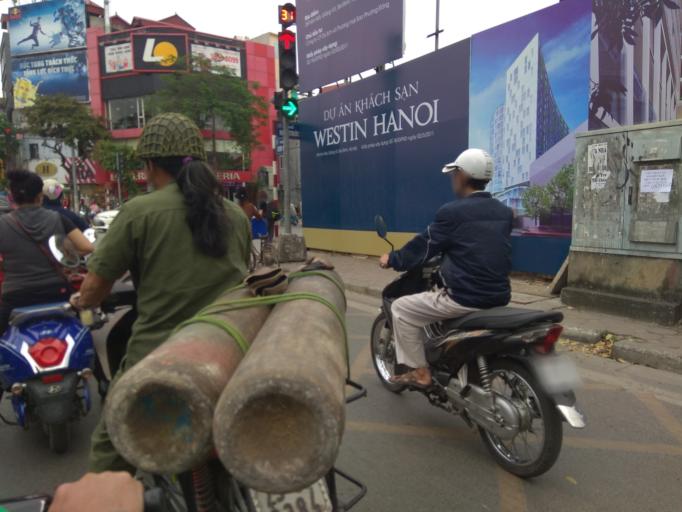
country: VN
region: Ha Noi
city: Dong Da
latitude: 21.0311
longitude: 105.8215
